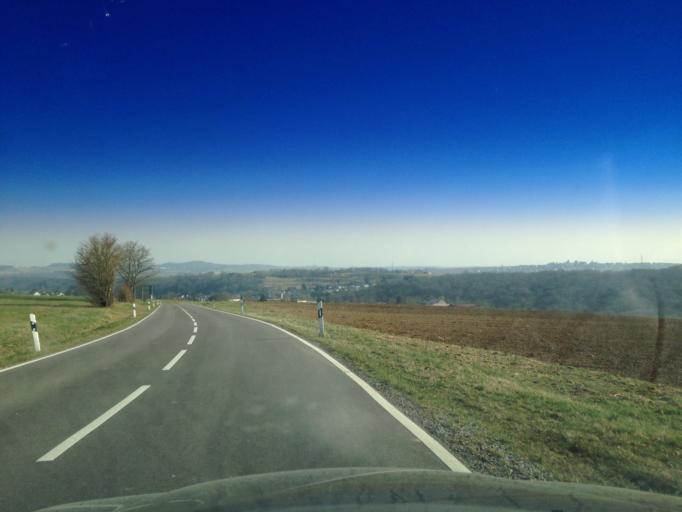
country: DE
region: Baden-Wuerttemberg
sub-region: Regierungsbezirk Stuttgart
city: Vaihingen an der Enz
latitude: 48.9217
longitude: 8.9316
